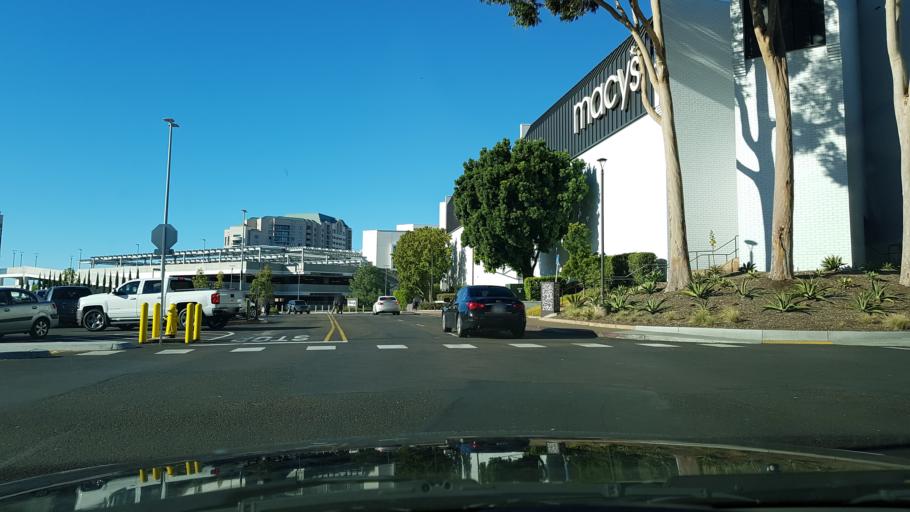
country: US
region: California
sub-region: San Diego County
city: La Jolla
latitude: 32.8684
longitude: -117.2122
